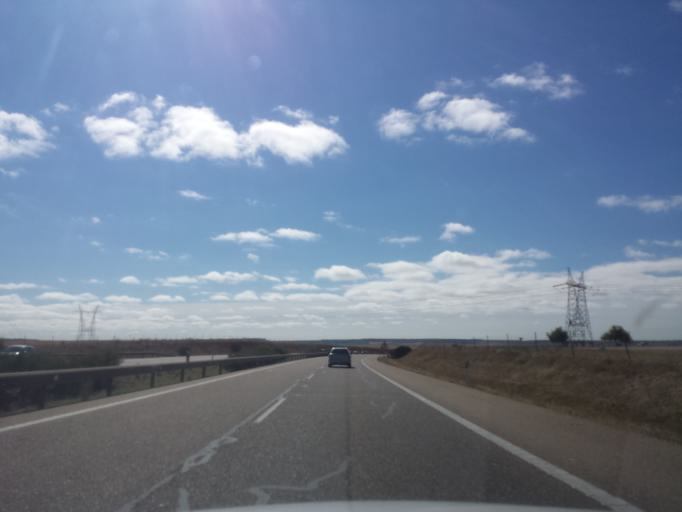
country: ES
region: Castille and Leon
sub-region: Provincia de Valladolid
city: San Pedro de Latarce
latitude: 41.7591
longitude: -5.2908
